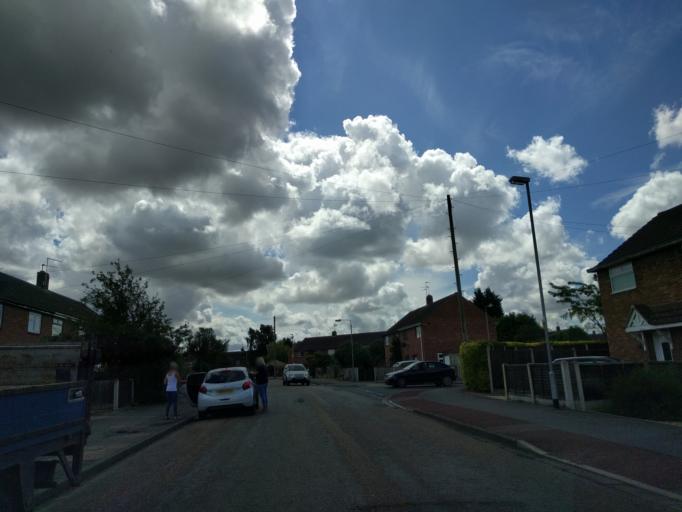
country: GB
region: England
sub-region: Nottinghamshire
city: Newark on Trent
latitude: 53.0599
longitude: -0.8114
